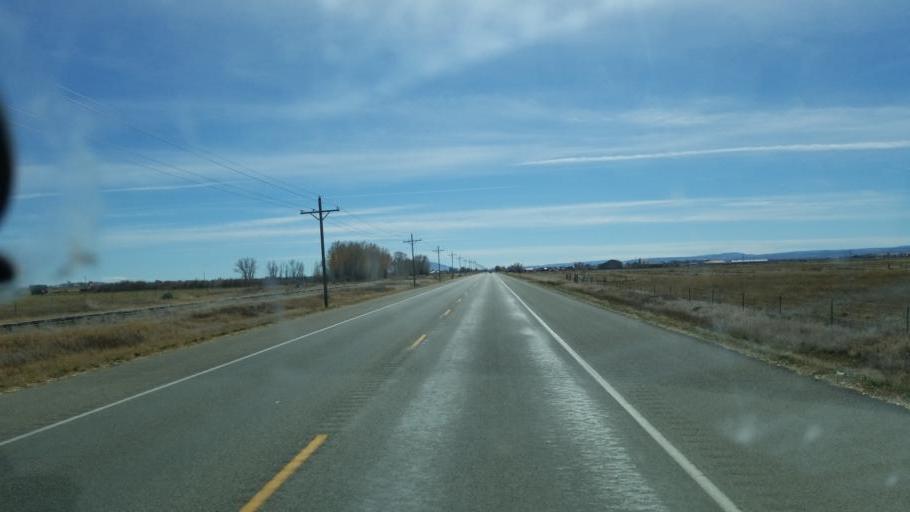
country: US
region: Colorado
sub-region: Conejos County
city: Conejos
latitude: 37.2010
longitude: -105.9808
